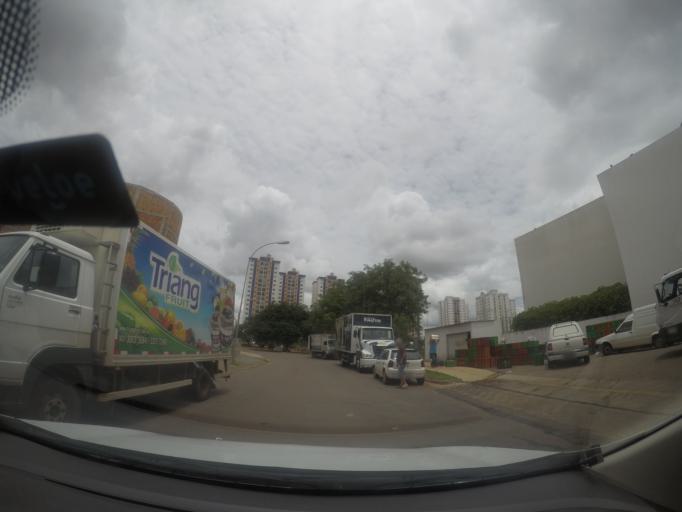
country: BR
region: Goias
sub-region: Goiania
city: Goiania
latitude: -16.7077
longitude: -49.3275
